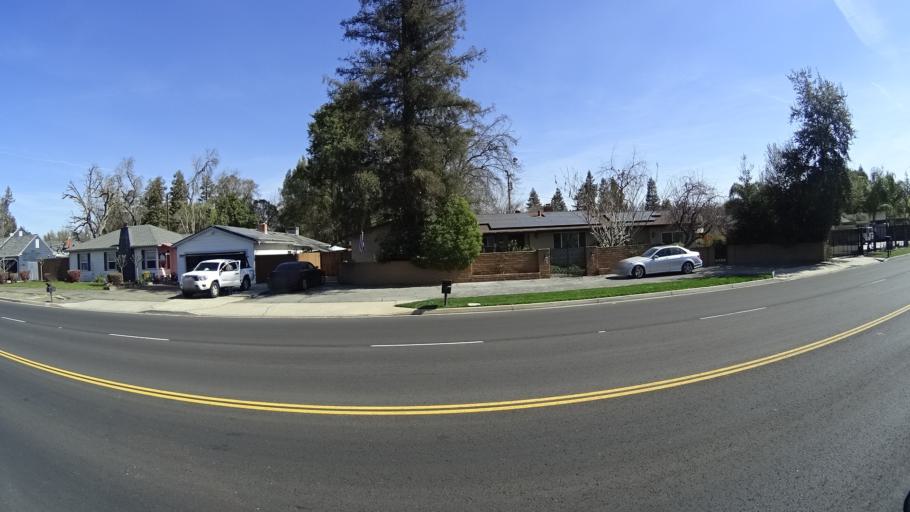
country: US
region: California
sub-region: Fresno County
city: Fresno
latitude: 36.8051
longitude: -119.8086
